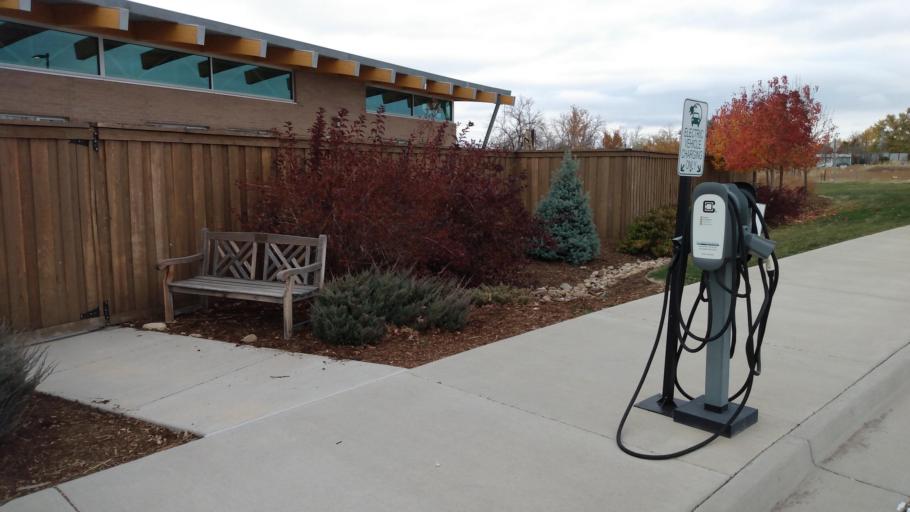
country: US
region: Colorado
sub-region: Boulder County
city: Boulder
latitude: 40.0137
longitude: -105.2104
